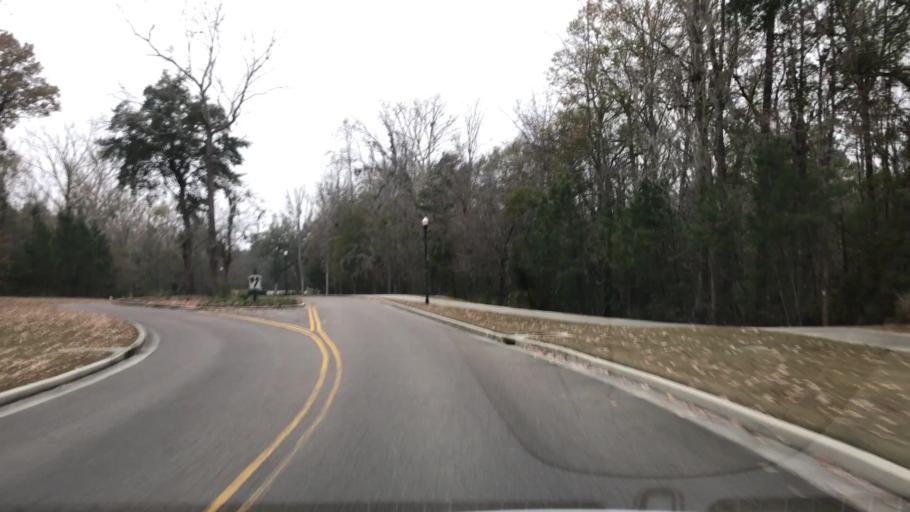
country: US
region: South Carolina
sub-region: Charleston County
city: Shell Point
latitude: 32.8071
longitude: -80.0781
